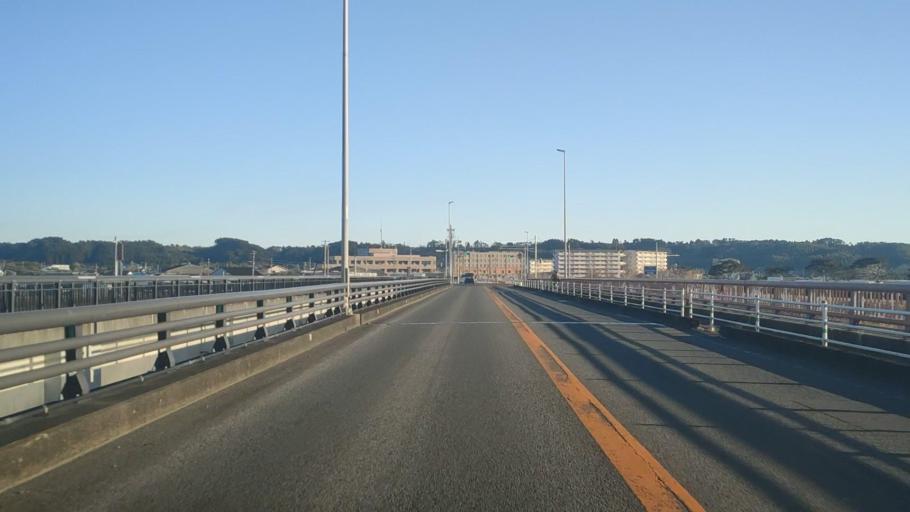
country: JP
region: Miyazaki
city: Takanabe
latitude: 32.1325
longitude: 131.5244
